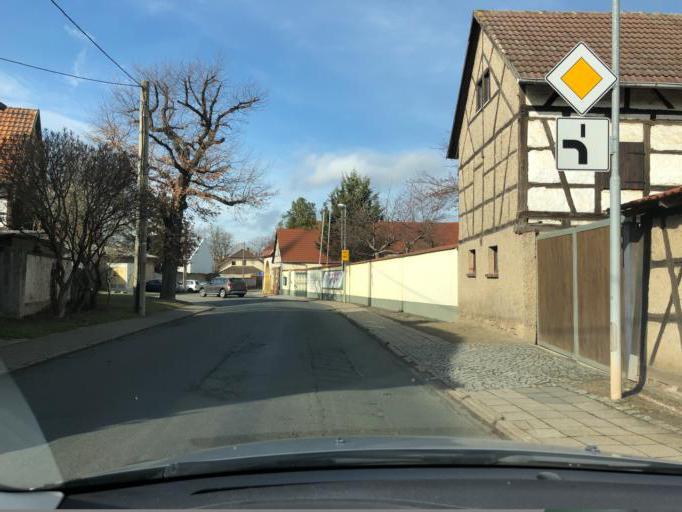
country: DE
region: Thuringia
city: Monchenholzhausen
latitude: 50.9799
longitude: 11.1004
